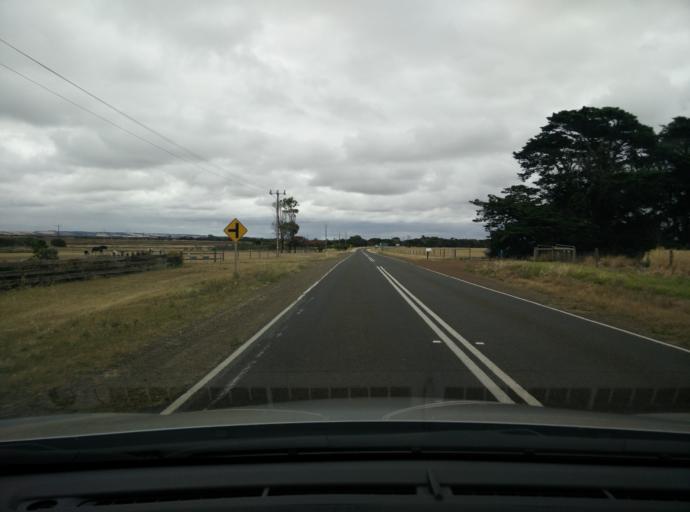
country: AU
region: South Australia
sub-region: Kangaroo Island
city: Kingscote
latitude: -35.6721
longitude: 137.5914
